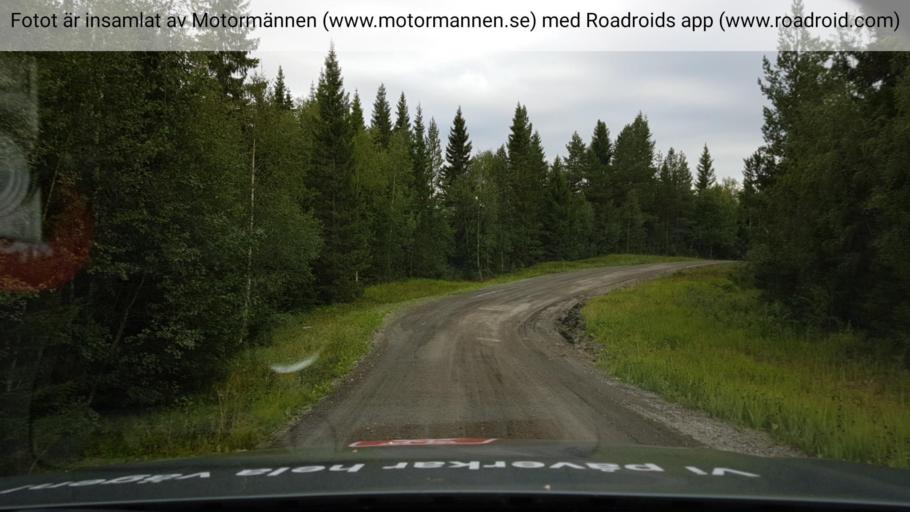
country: SE
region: Jaemtland
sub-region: Krokoms Kommun
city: Valla
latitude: 63.4056
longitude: 14.0858
